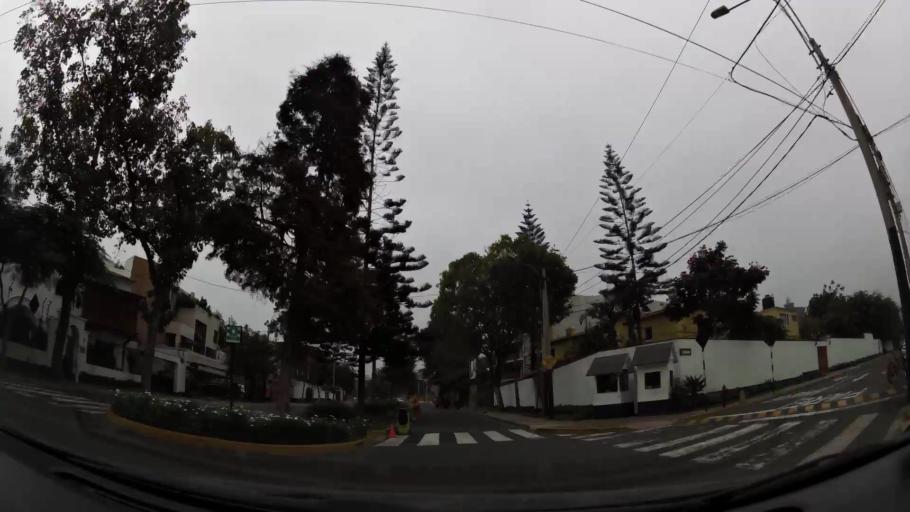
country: PE
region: Lima
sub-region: Lima
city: San Isidro
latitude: -12.0987
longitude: -77.0419
